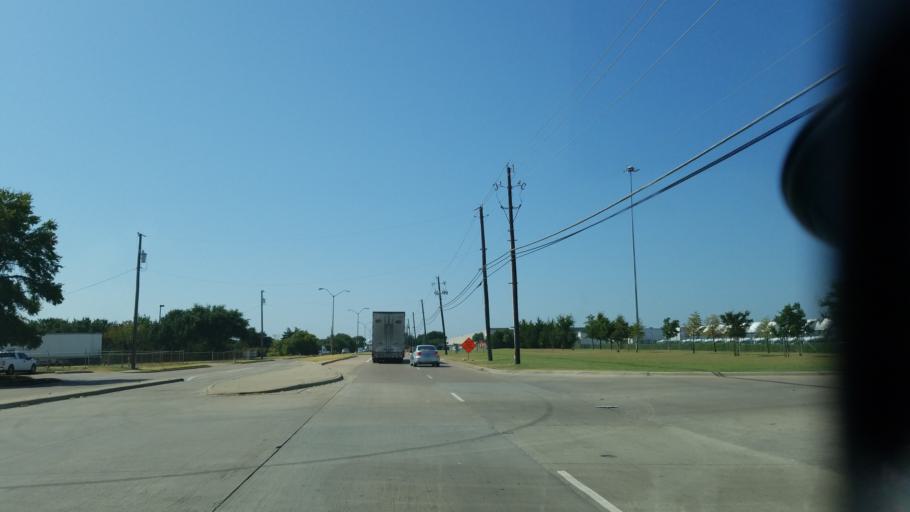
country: US
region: Texas
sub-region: Dallas County
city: Cockrell Hill
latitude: 32.7033
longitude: -96.9087
